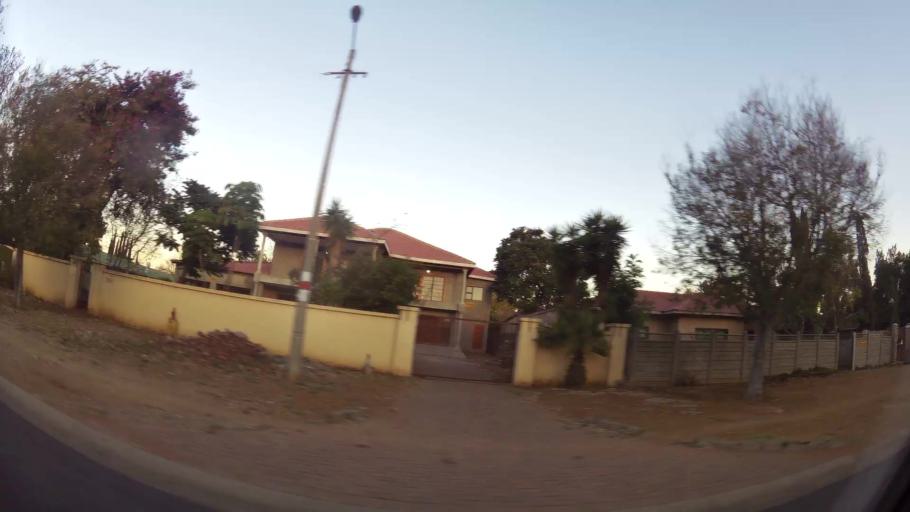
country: ZA
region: North-West
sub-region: Bojanala Platinum District Municipality
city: Rustenburg
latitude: -25.6711
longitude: 27.2261
